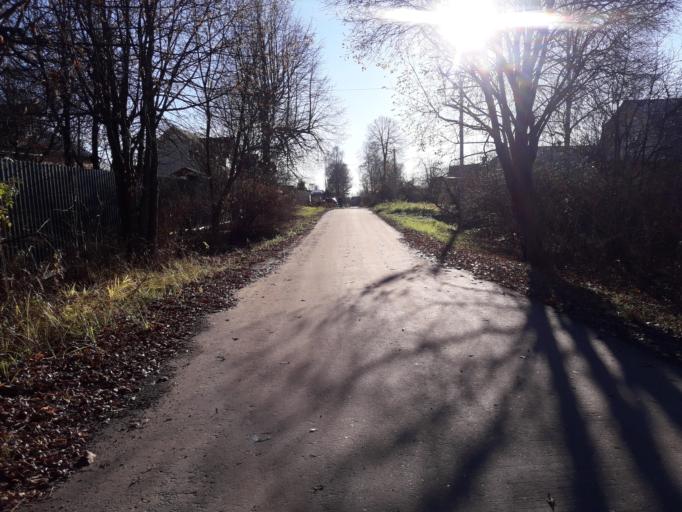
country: RU
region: Moskovskaya
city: Ashukino
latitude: 56.1661
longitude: 37.9656
